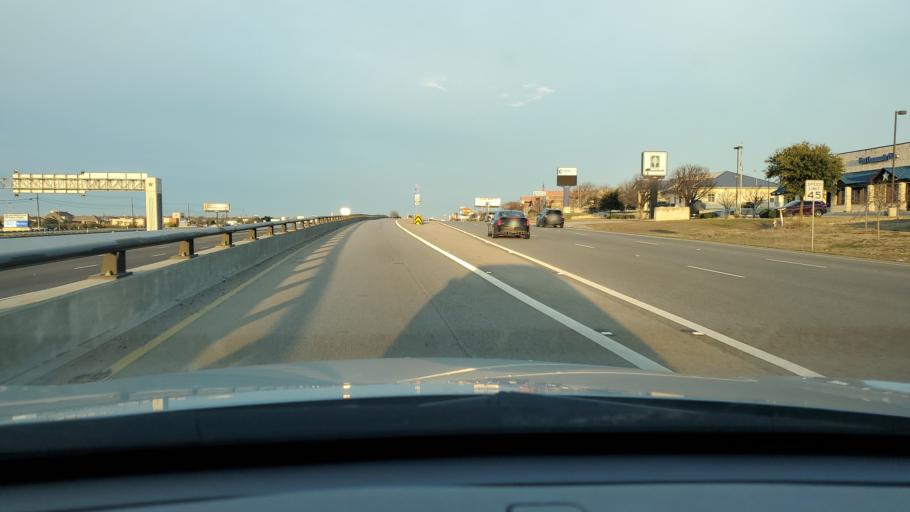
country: US
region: Texas
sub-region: Bell County
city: Harker Heights
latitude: 31.0741
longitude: -97.6804
